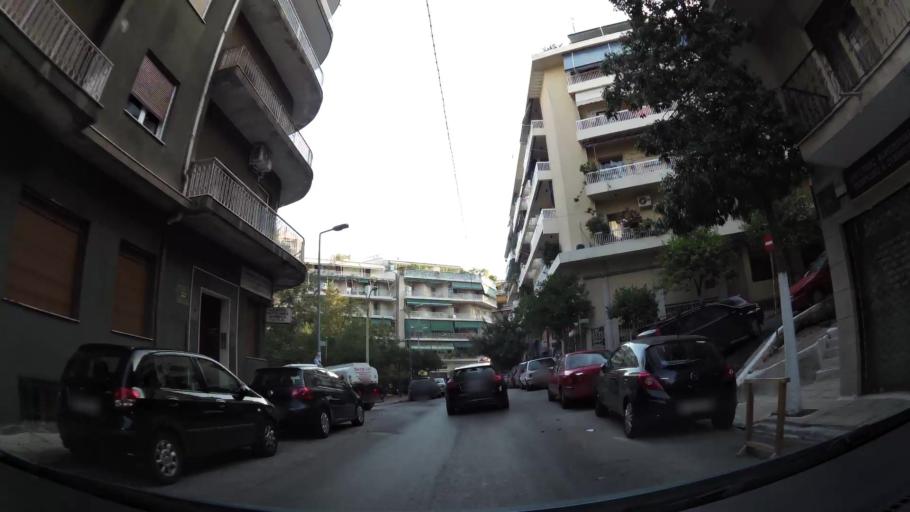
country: GR
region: Attica
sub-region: Nomarchia Athinas
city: Kaisariani
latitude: 37.9796
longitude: 23.7594
